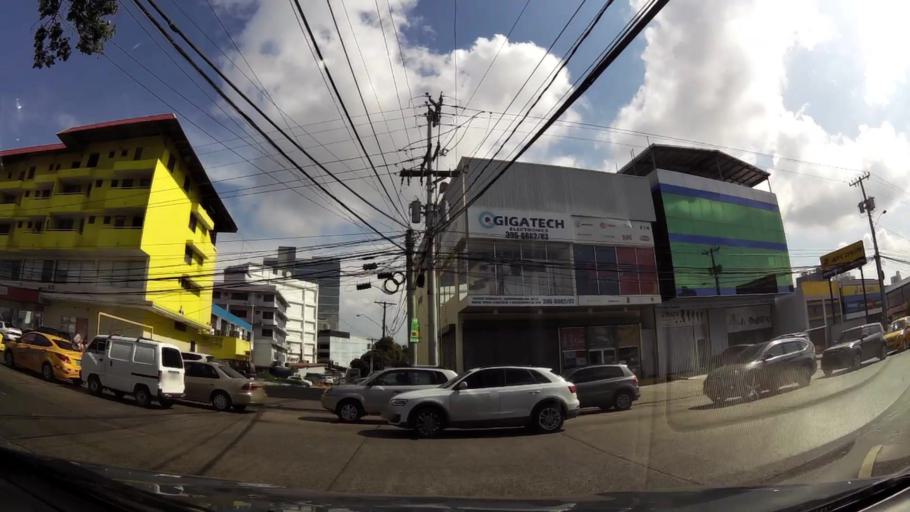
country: PA
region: Panama
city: Panama
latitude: 9.0000
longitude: -79.5239
